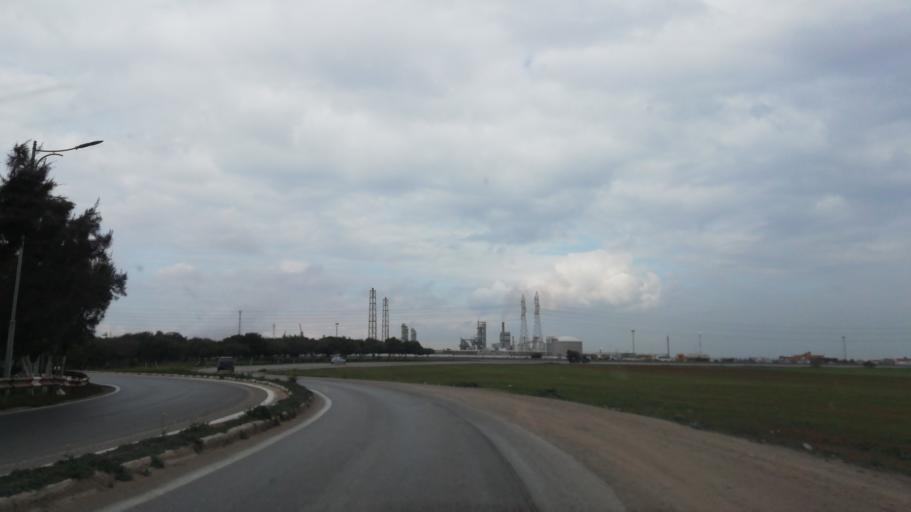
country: DZ
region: Oran
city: Ain el Bya
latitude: 35.7977
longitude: -0.3441
